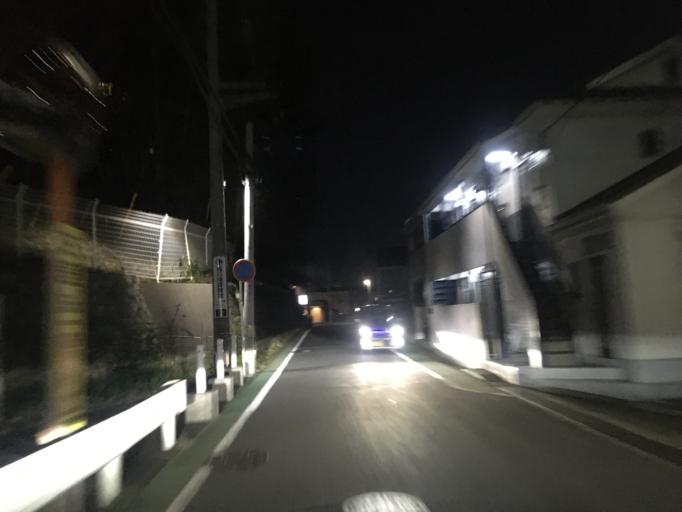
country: JP
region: Tokyo
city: Chofugaoka
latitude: 35.6065
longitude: 139.5206
